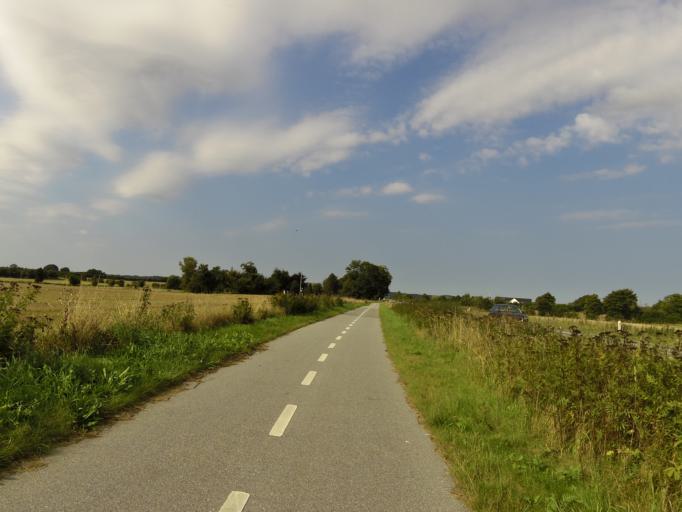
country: DK
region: South Denmark
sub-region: Vejen Kommune
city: Vejen
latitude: 55.4272
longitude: 9.1468
